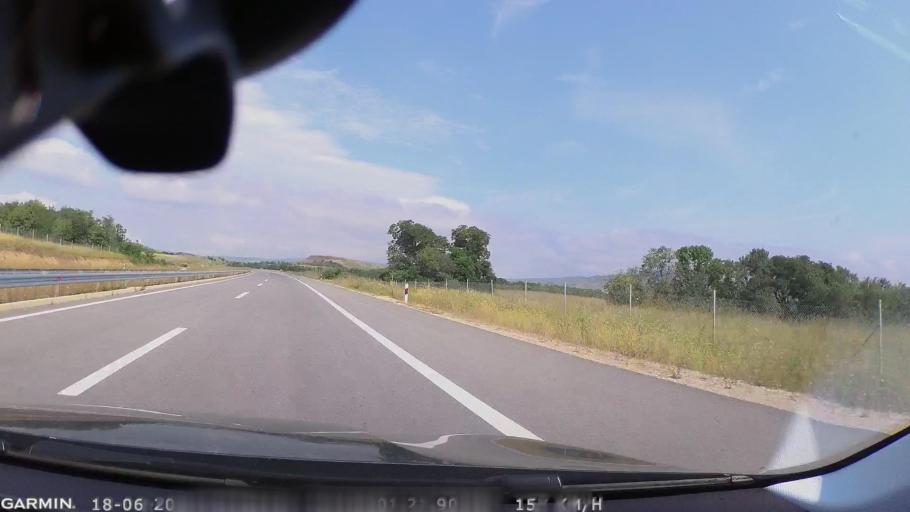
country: MK
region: Sveti Nikole
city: Gorobinci
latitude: 41.9110
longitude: 21.8999
